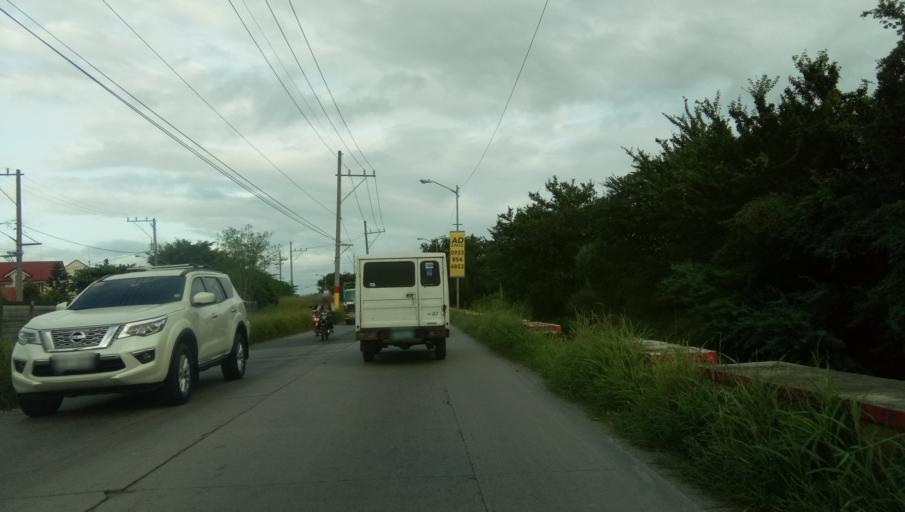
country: PH
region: Calabarzon
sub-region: Province of Cavite
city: Dasmarinas
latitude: 14.3677
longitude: 120.9320
